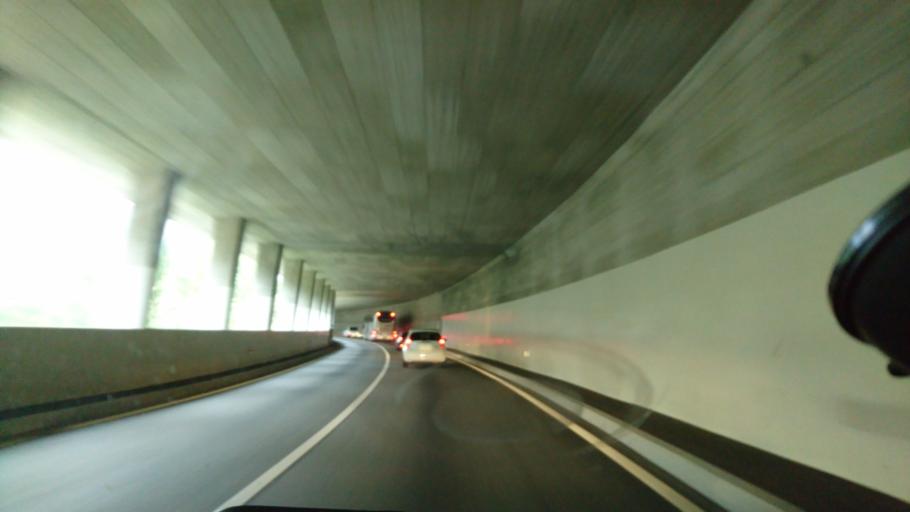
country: IT
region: Piedmont
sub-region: Provincia Verbano-Cusio-Ossola
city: Trasquera
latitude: 46.1988
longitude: 8.1344
